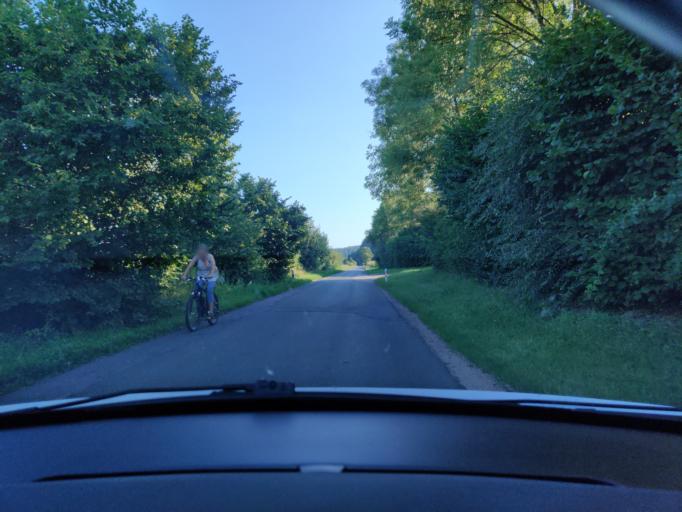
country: DE
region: Bavaria
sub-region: Upper Palatinate
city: Nabburg
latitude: 49.4367
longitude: 12.1715
